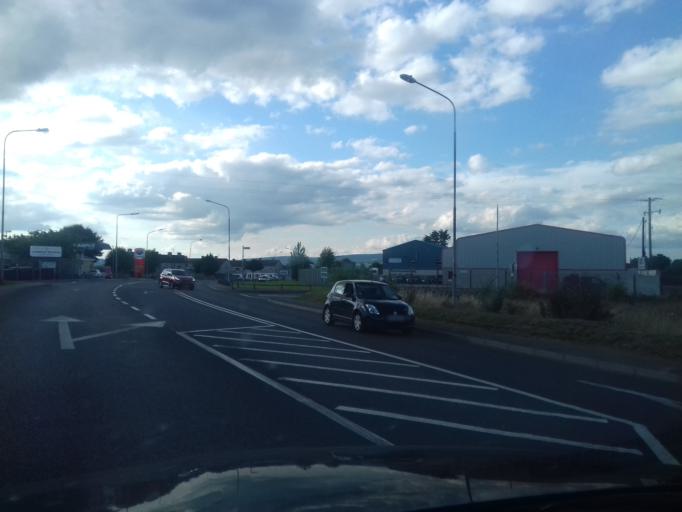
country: IE
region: Leinster
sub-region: Loch Garman
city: New Ross
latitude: 52.3916
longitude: -6.9325
